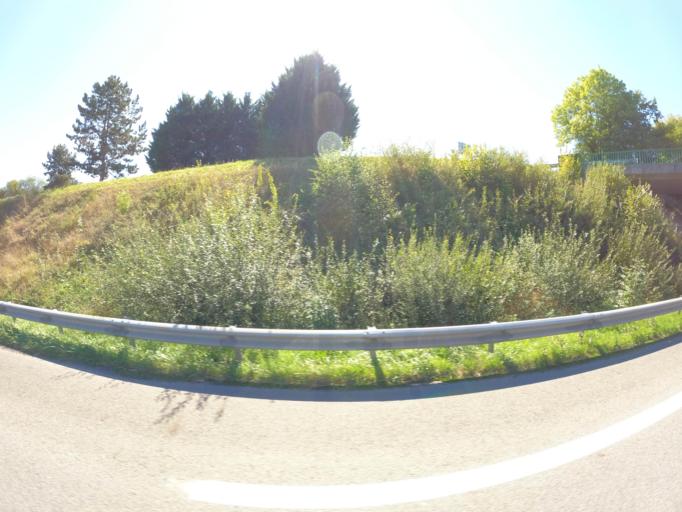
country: FR
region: Limousin
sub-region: Departement de la Creuse
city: Saint-Maurice-la-Souterraine
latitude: 46.2168
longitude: 1.4314
